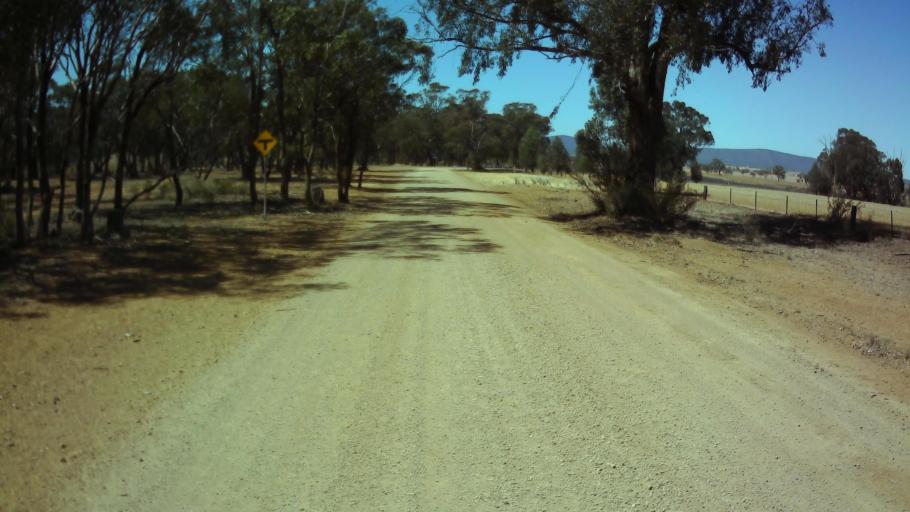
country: AU
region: New South Wales
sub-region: Weddin
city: Grenfell
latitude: -33.8688
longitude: 148.0878
